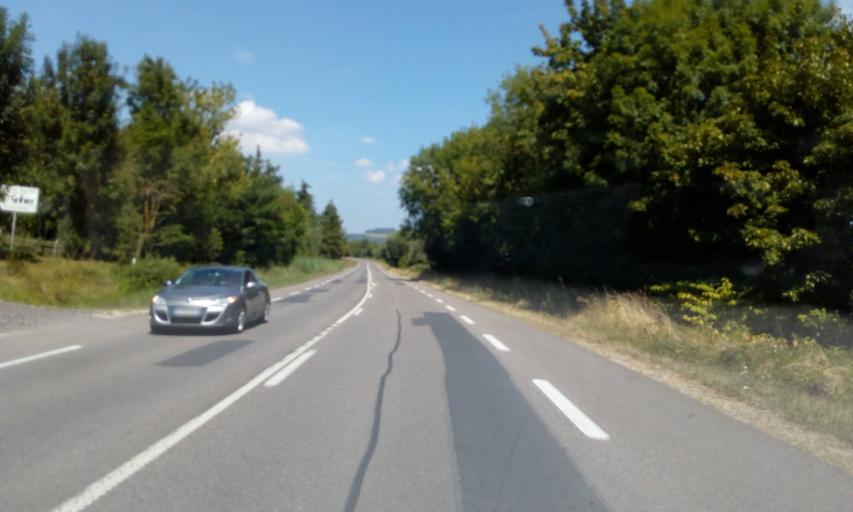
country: FR
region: Lorraine
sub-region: Departement de Meurthe-et-Moselle
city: Dieulouard
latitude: 48.8556
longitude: 6.0756
